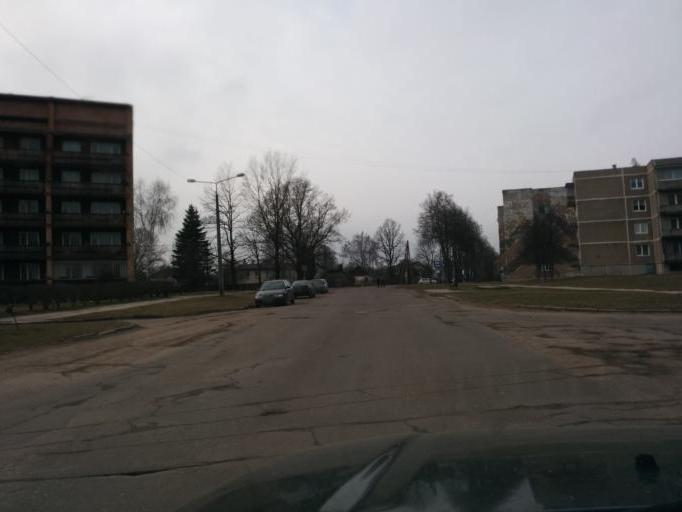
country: LV
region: Ozolnieku
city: Ozolnieki
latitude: 56.6661
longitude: 23.7630
